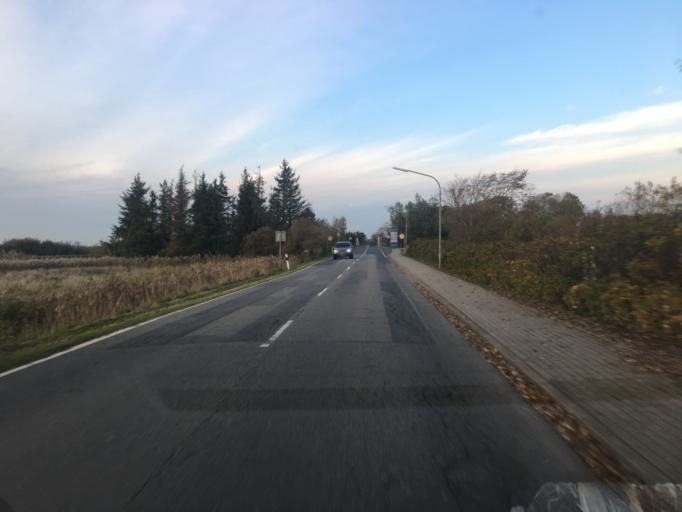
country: DE
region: Schleswig-Holstein
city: Aventoft
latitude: 54.9053
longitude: 8.8321
